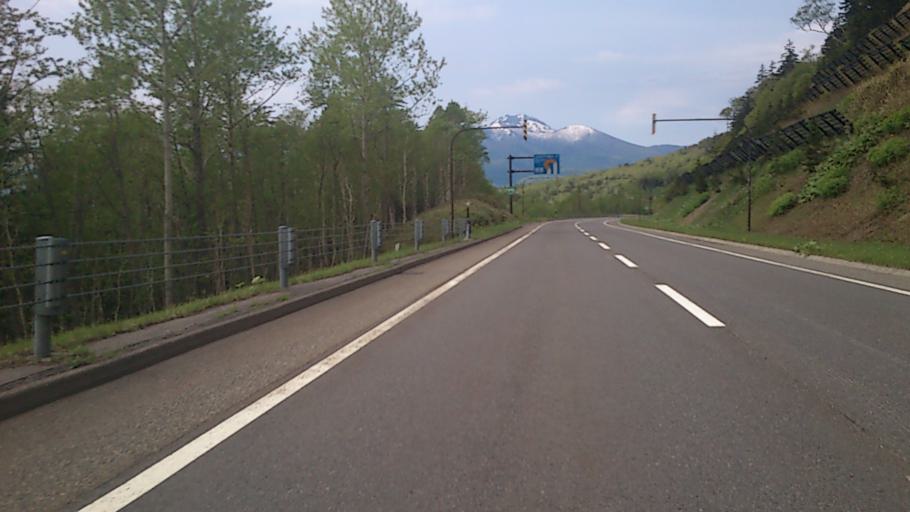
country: JP
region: Hokkaido
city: Kamikawa
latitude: 43.5741
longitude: 143.1239
